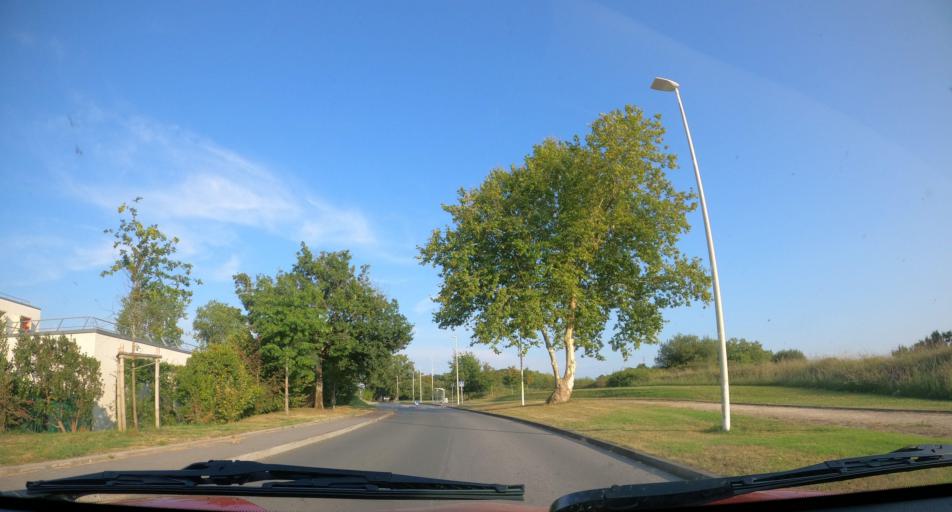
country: FR
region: Aquitaine
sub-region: Departement des Pyrenees-Atlantiques
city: Boucau
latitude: 43.5077
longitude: -1.4351
